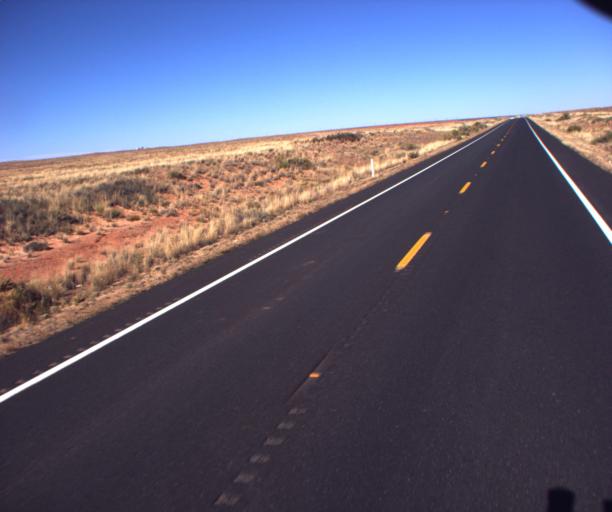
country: US
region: Arizona
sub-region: Coconino County
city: Kaibito
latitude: 36.3717
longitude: -110.8946
